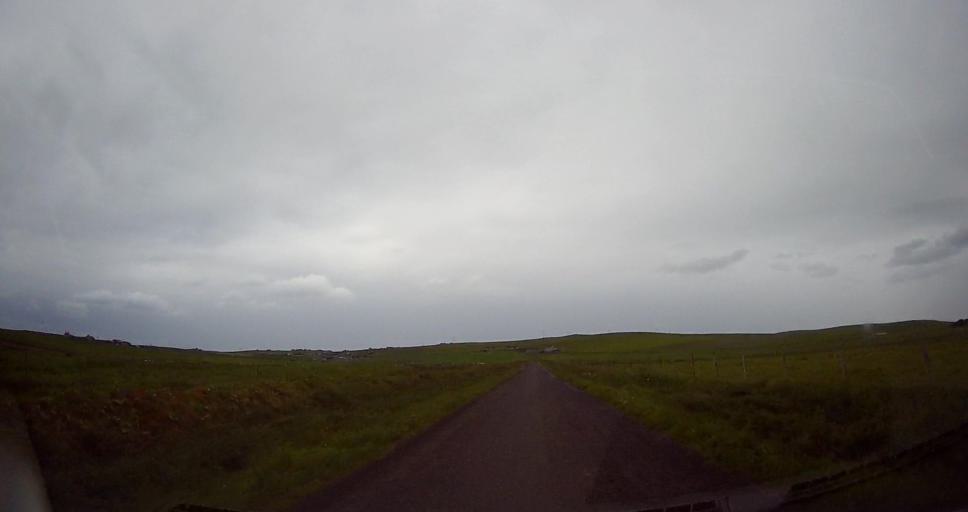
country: GB
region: Scotland
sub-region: Orkney Islands
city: Stromness
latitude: 59.0696
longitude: -3.2837
